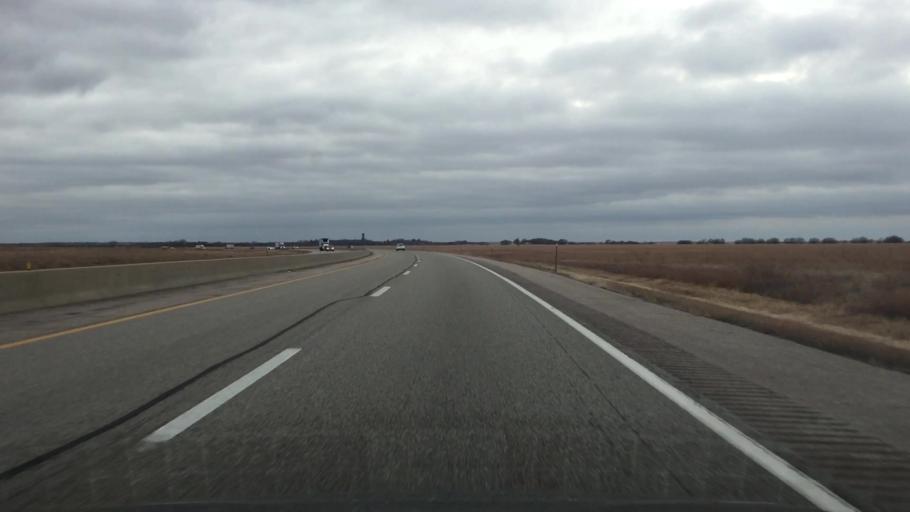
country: US
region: Kansas
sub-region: Butler County
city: El Dorado
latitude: 37.9034
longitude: -96.8270
